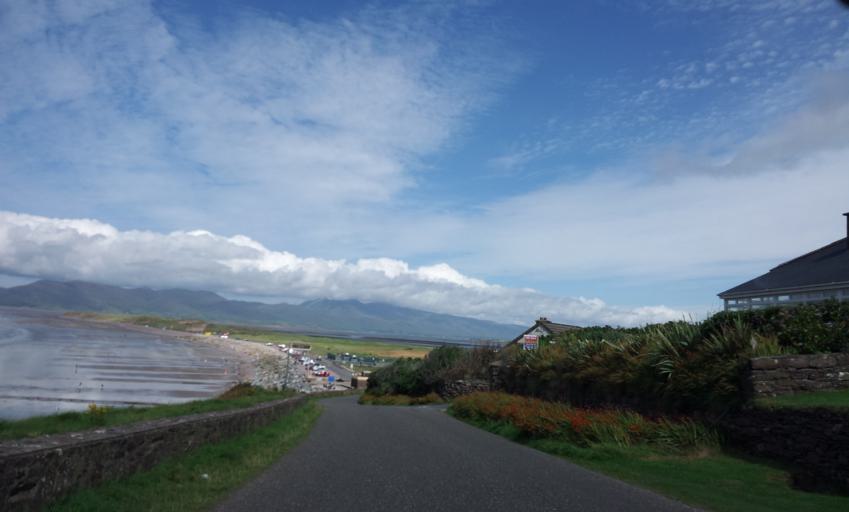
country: IE
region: Munster
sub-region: Ciarrai
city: Killorglin
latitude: 52.0526
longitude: -9.9780
